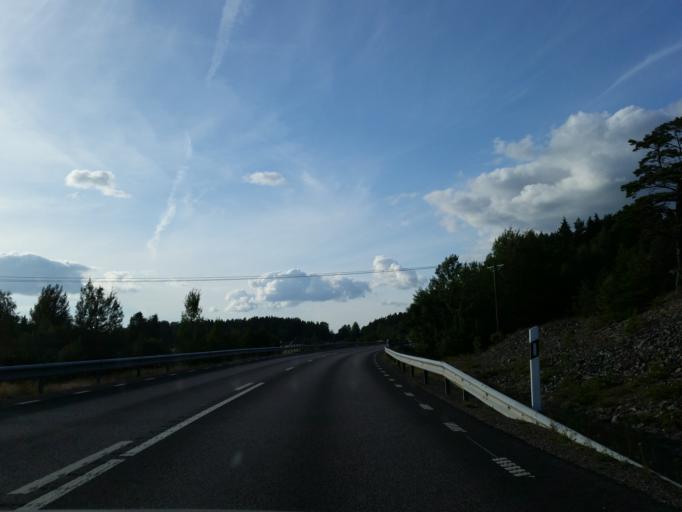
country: SE
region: Soedermanland
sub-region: Gnesta Kommun
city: Gnesta
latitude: 59.0399
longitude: 17.2954
